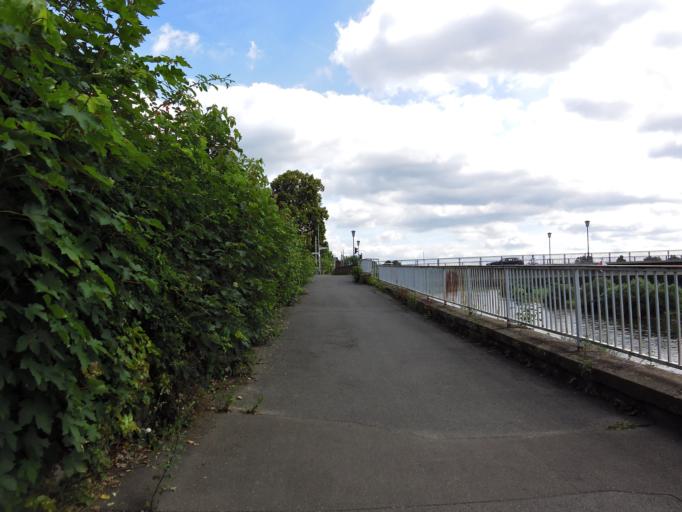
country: DE
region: North Rhine-Westphalia
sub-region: Regierungsbezirk Detmold
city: Hoexter
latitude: 51.7727
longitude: 9.3823
